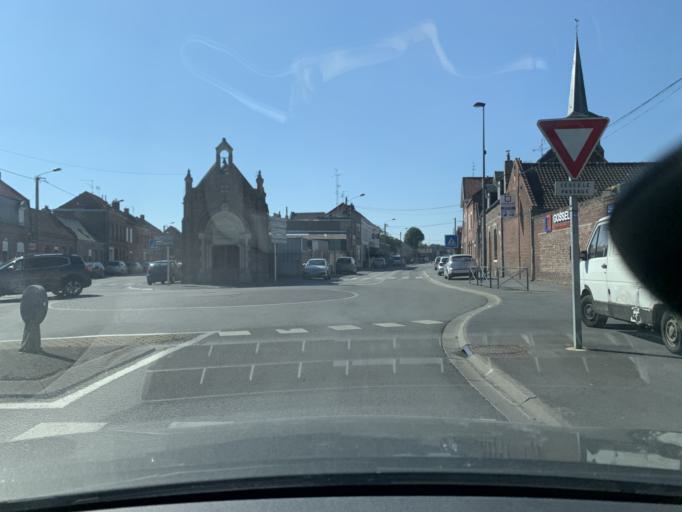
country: FR
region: Nord-Pas-de-Calais
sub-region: Departement du Nord
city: Cambrai
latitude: 50.1626
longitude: 3.2410
